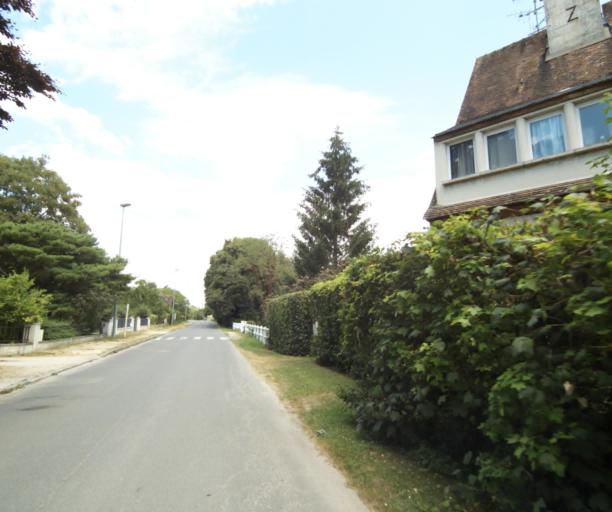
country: FR
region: Ile-de-France
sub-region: Departement de Seine-et-Marne
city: Hericy
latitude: 48.4533
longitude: 2.7595
